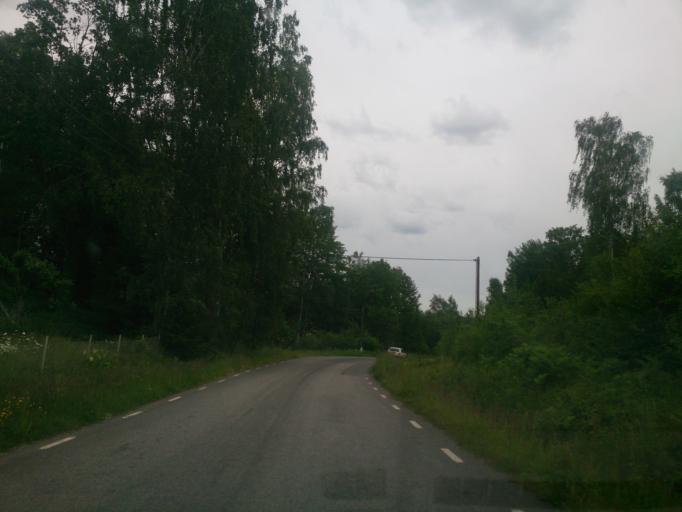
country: SE
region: OEstergoetland
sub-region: Valdemarsviks Kommun
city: Gusum
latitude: 58.3297
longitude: 16.4219
